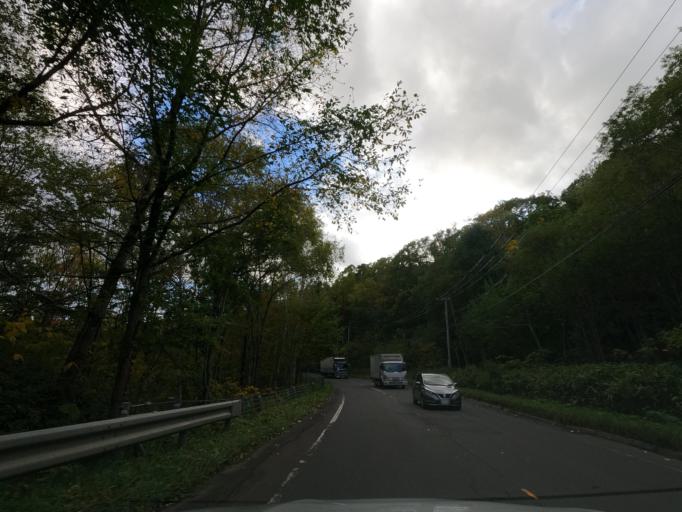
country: JP
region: Hokkaido
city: Date
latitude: 42.6603
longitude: 141.0690
